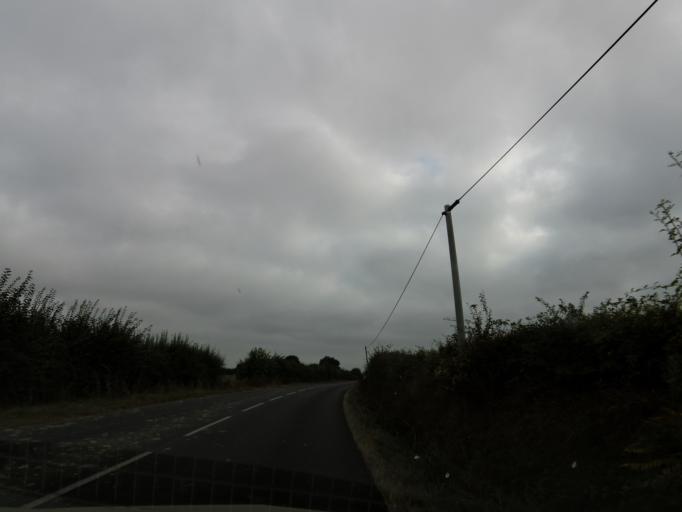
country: FR
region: Pays de la Loire
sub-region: Departement de la Vendee
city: Moutiers-les-Mauxfaits
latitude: 46.4799
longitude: -1.4437
